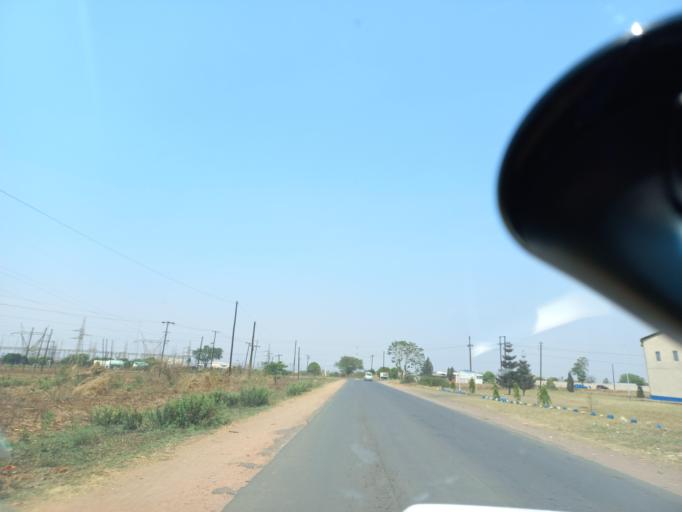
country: ZM
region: Lusaka
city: Kafue
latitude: -15.7496
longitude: 28.1634
